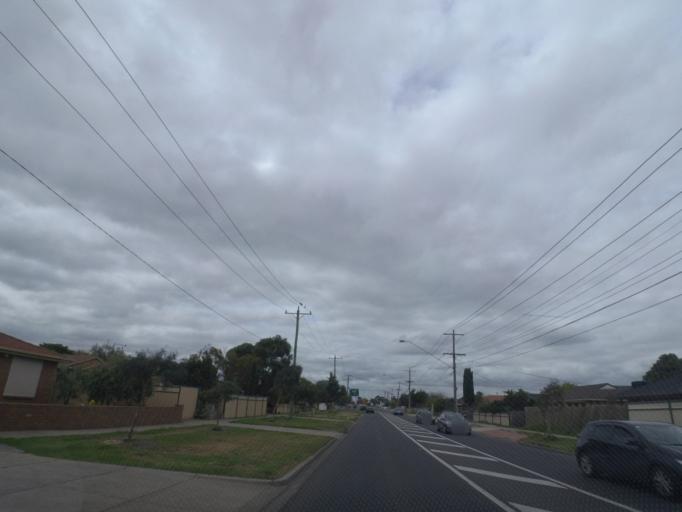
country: AU
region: Victoria
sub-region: Brimbank
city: Delahey
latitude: -37.7272
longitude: 144.7787
